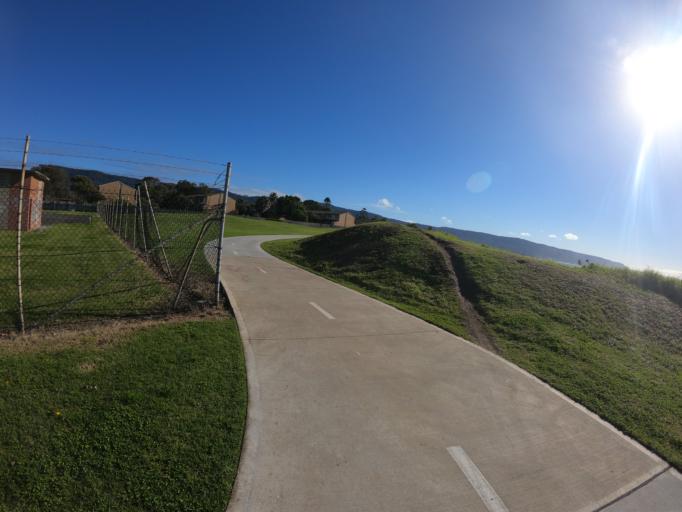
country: AU
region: New South Wales
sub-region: Wollongong
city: East Corrimal
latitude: -34.3689
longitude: 150.9246
